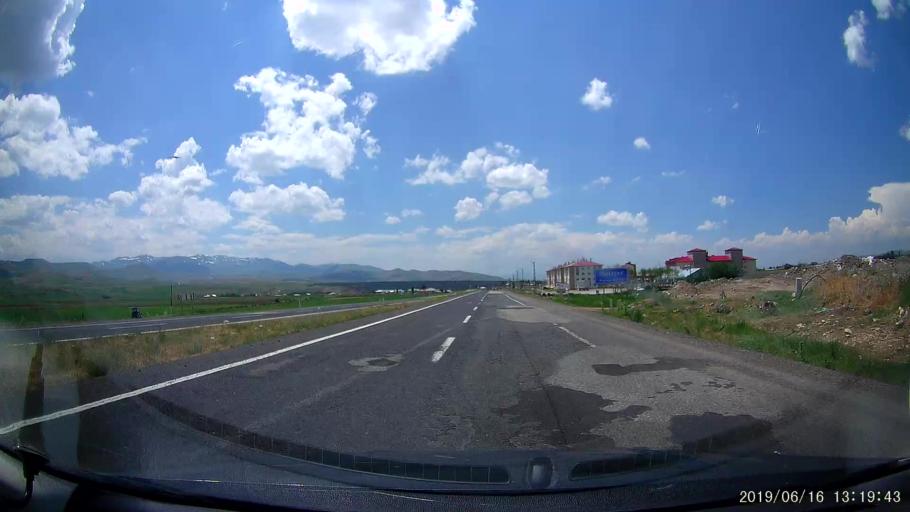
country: TR
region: Agri
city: Taslicay
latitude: 39.6328
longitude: 43.4003
